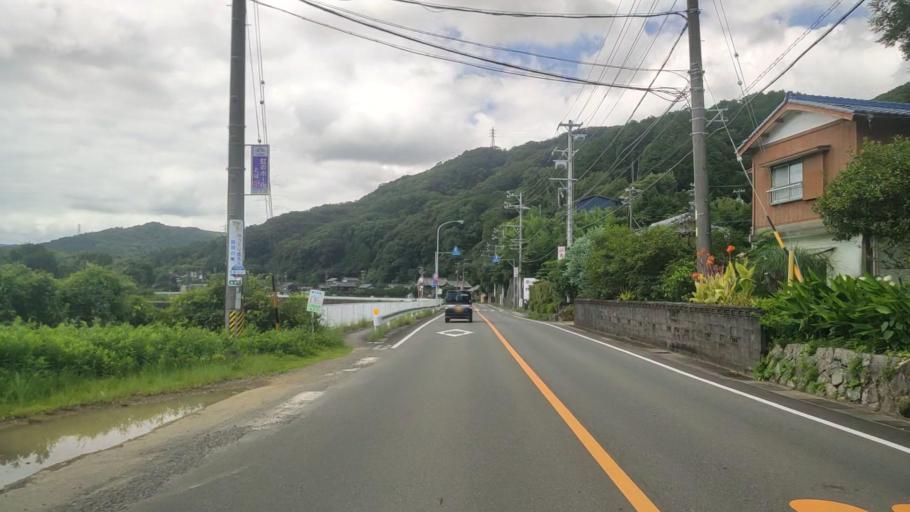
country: JP
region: Mie
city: Toba
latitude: 34.4544
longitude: 136.8407
